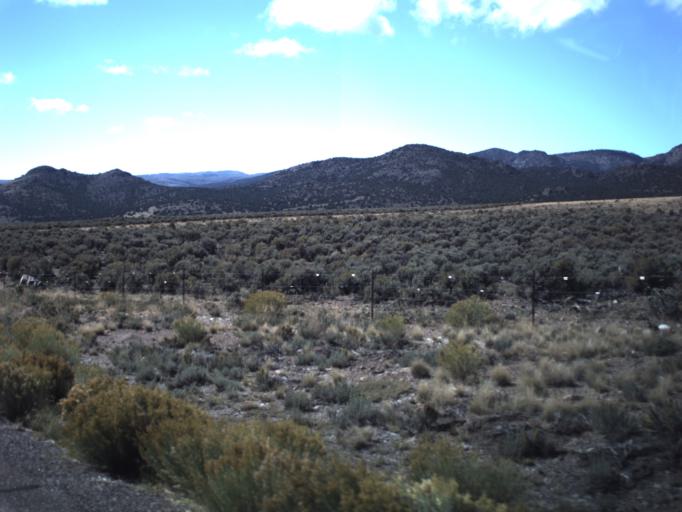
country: US
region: Utah
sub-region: Piute County
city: Junction
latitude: 38.3316
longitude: -111.9576
